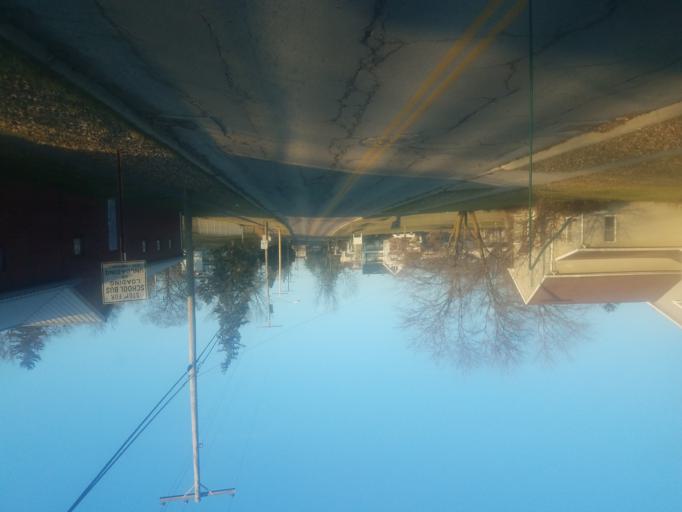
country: US
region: Ohio
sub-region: Crawford County
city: Bucyrus
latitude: 40.8138
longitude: -82.9718
